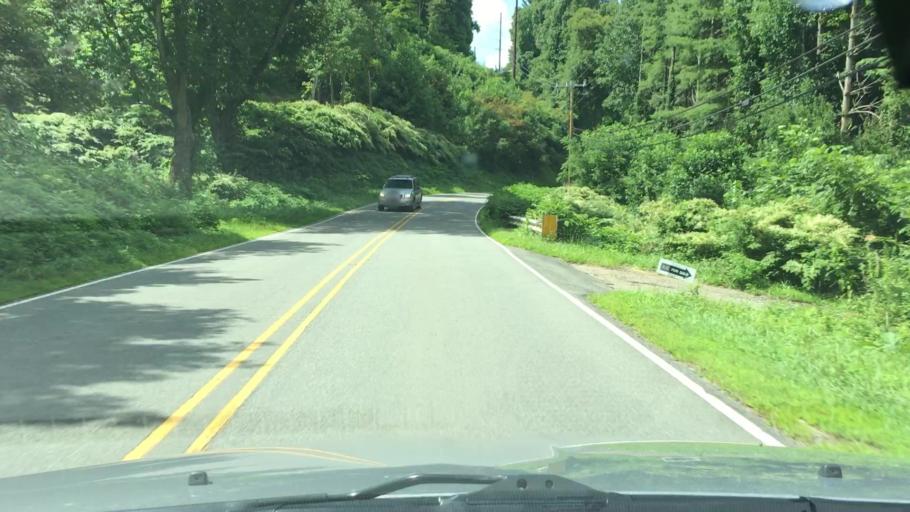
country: US
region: North Carolina
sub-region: Yancey County
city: Burnsville
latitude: 35.8655
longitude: -82.2030
